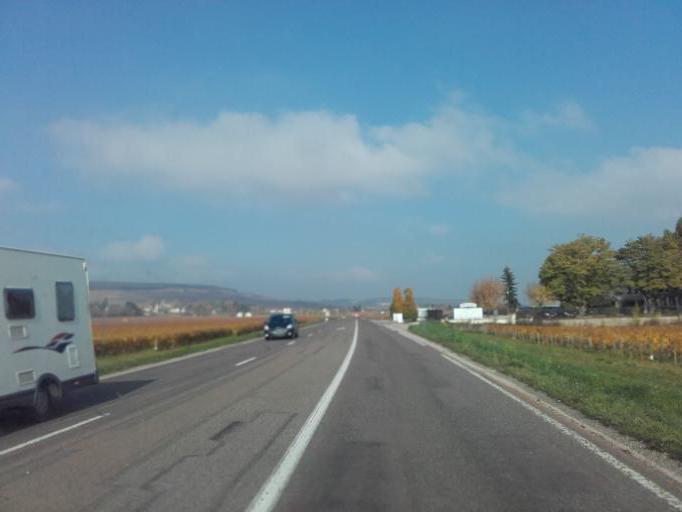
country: FR
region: Bourgogne
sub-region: Departement de la Cote-d'Or
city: Beaune
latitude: 47.0516
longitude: 4.8562
